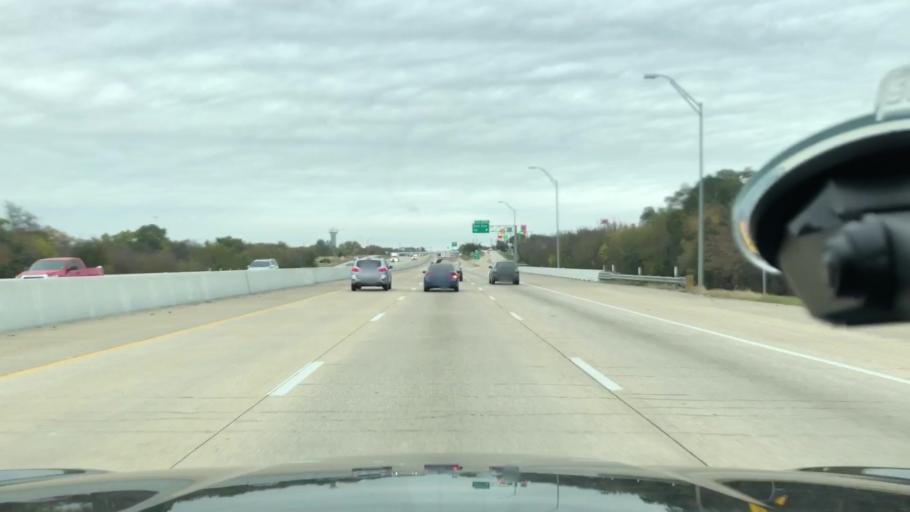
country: US
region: Texas
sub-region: Ellis County
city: Red Oak
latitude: 32.5099
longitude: -96.8220
